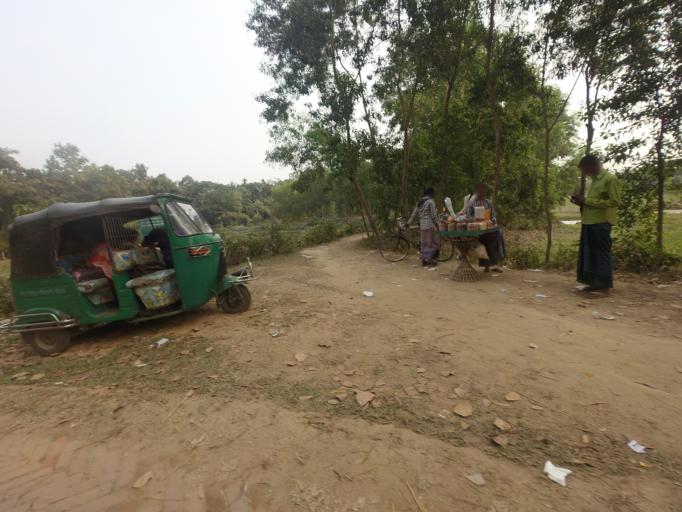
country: BD
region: Dhaka
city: Netrakona
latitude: 25.1716
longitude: 90.6573
